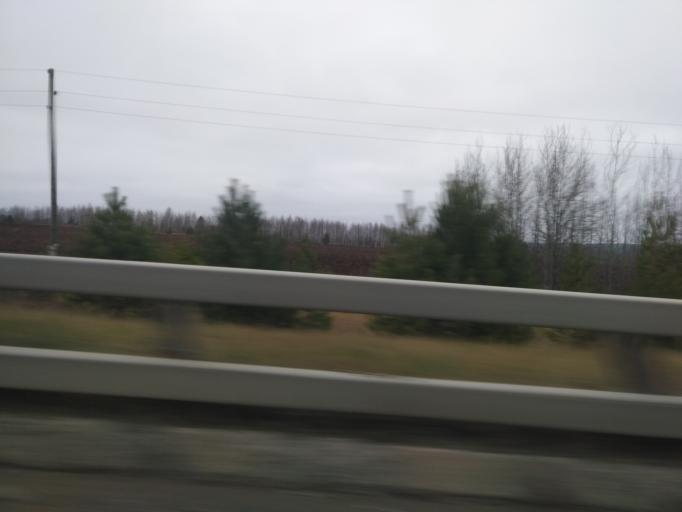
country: RU
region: Kirov
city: Krasnaya Polyana
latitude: 56.2292
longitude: 51.2110
